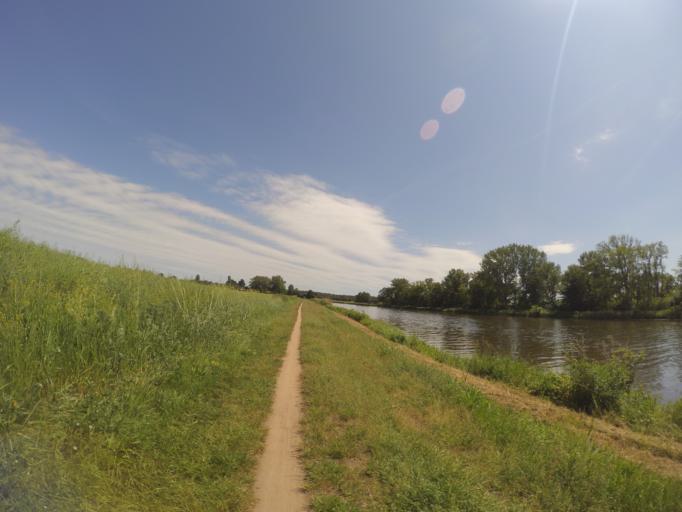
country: CZ
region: Central Bohemia
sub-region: Okres Nymburk
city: Sadska
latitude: 50.1662
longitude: 14.9559
